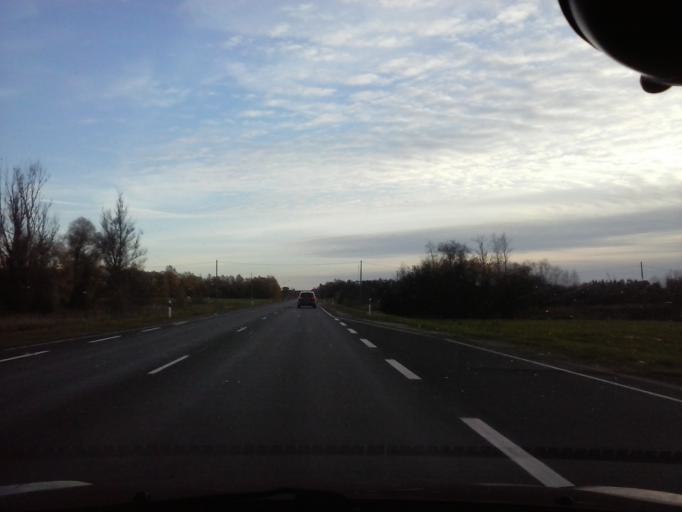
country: EE
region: Harju
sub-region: Nissi vald
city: Turba
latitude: 58.9178
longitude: 24.1126
